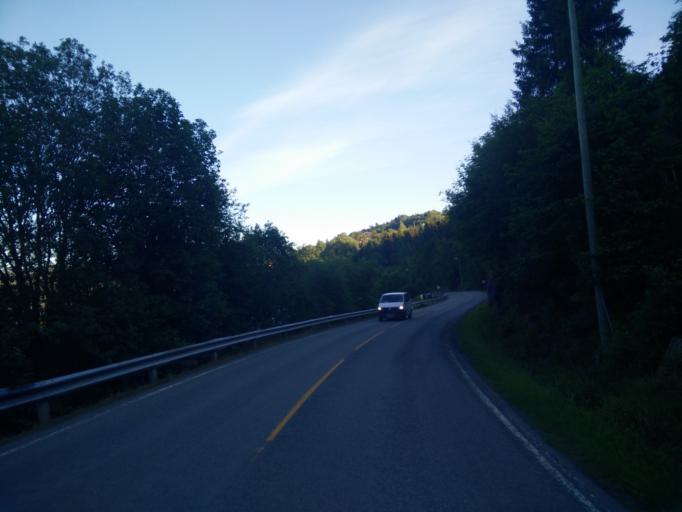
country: NO
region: Sor-Trondelag
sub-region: Skaun
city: Borsa
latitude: 63.3411
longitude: 10.0571
